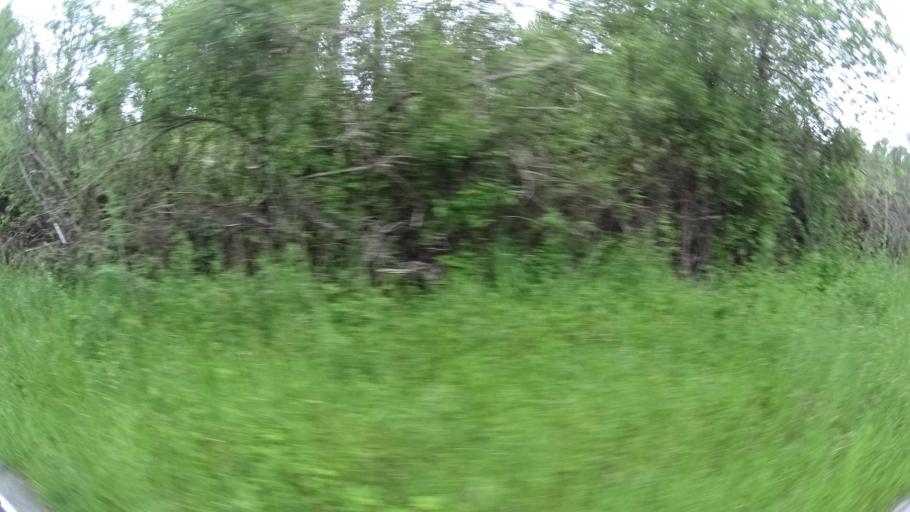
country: US
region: California
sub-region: Humboldt County
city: Blue Lake
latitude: 40.8698
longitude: -123.9945
